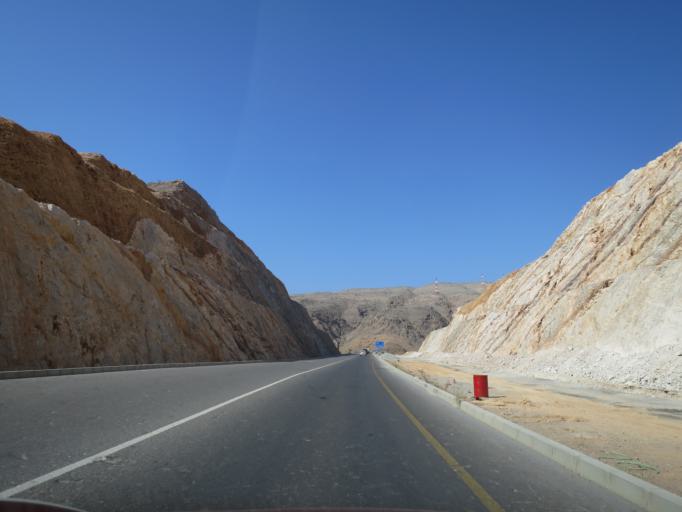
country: OM
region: Muhafazat Masqat
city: Muscat
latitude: 23.5202
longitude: 58.6330
